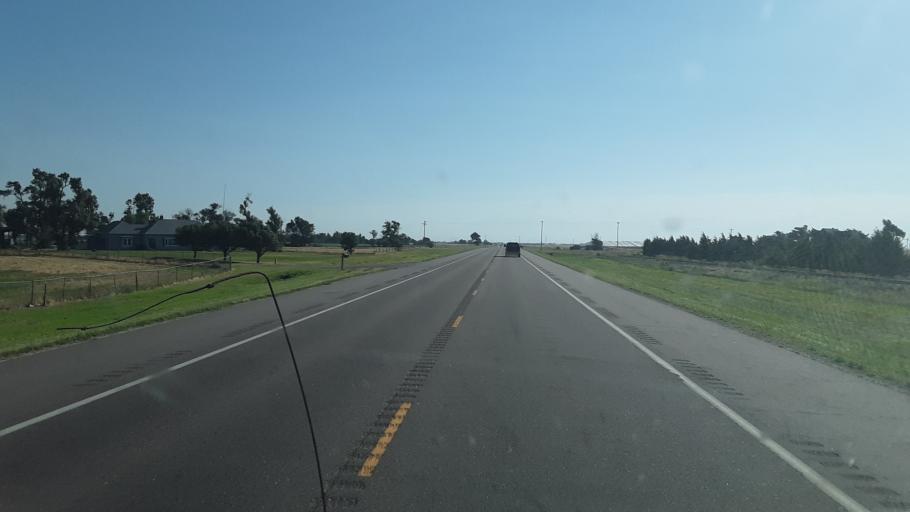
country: US
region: Kansas
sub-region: Pawnee County
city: Larned
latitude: 38.1982
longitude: -99.0723
